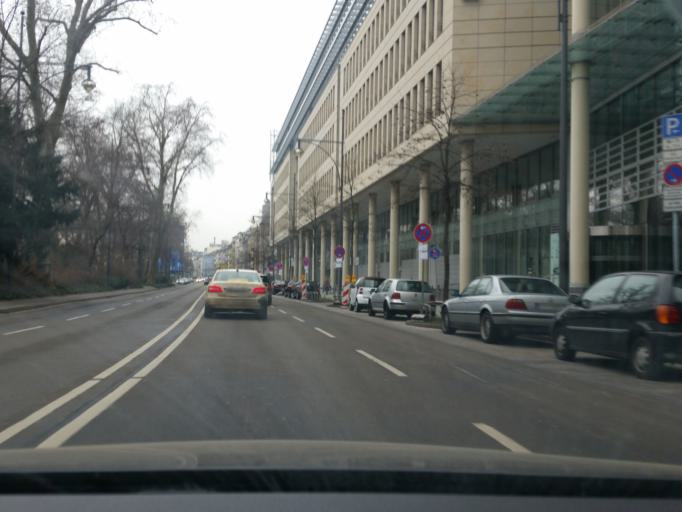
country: DE
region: Hesse
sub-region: Regierungsbezirk Darmstadt
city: Frankfurt am Main
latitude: 50.1173
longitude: 8.6711
